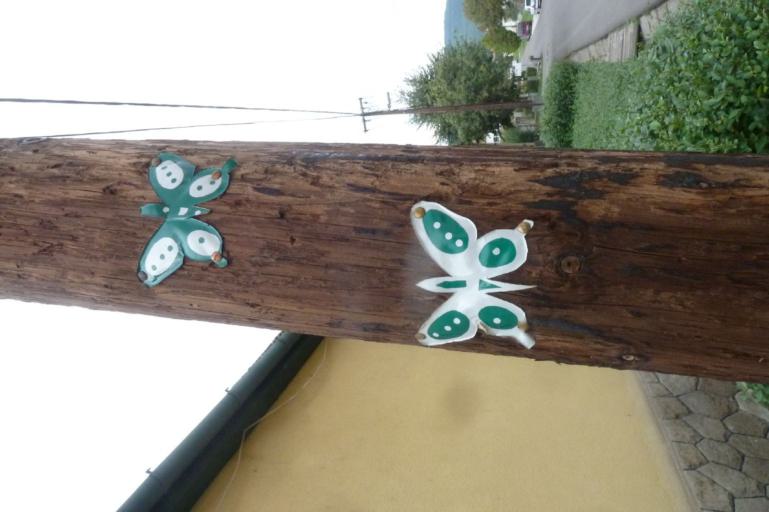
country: HU
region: Pest
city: Kismaros
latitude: 47.8663
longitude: 19.0009
